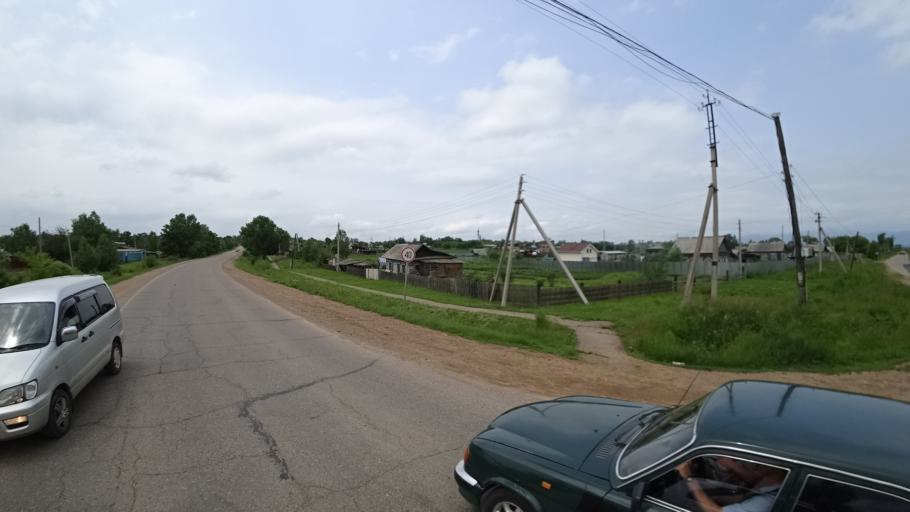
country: RU
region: Primorskiy
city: Novosysoyevka
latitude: 44.2313
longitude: 133.3715
